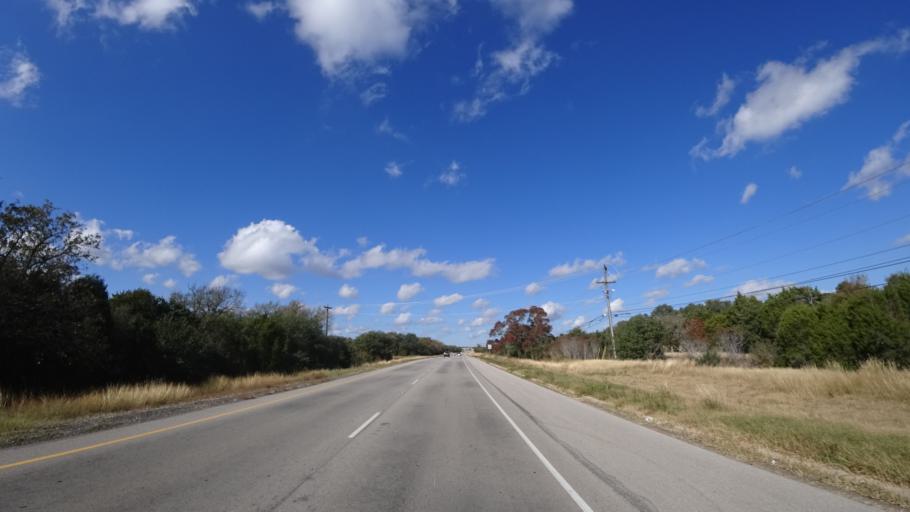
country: US
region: Texas
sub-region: Travis County
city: Shady Hollow
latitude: 30.1891
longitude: -97.9164
